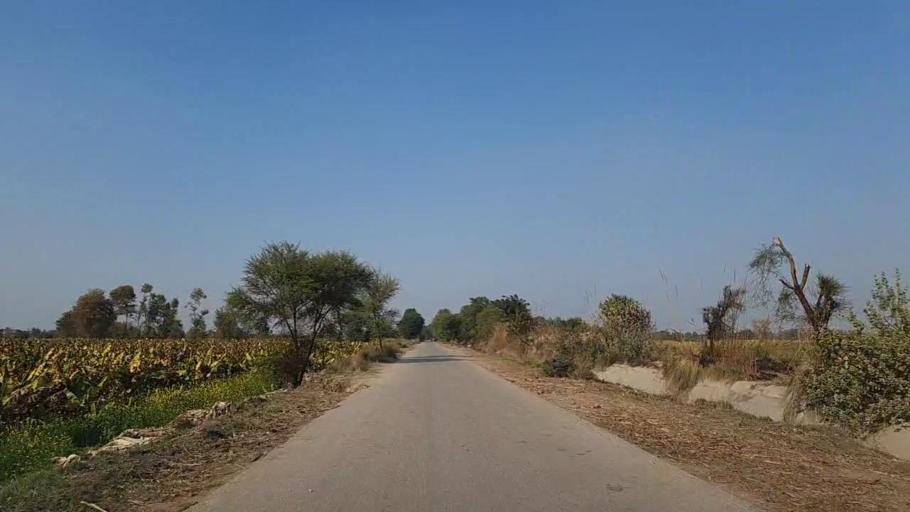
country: PK
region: Sindh
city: Daur
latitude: 26.4098
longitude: 68.2592
